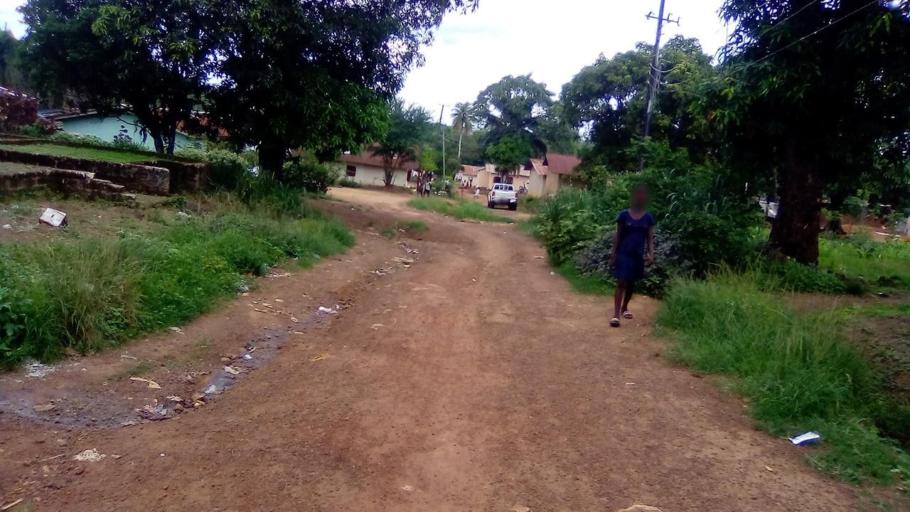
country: SL
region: Southern Province
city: Bo
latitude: 7.9604
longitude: -11.7234
